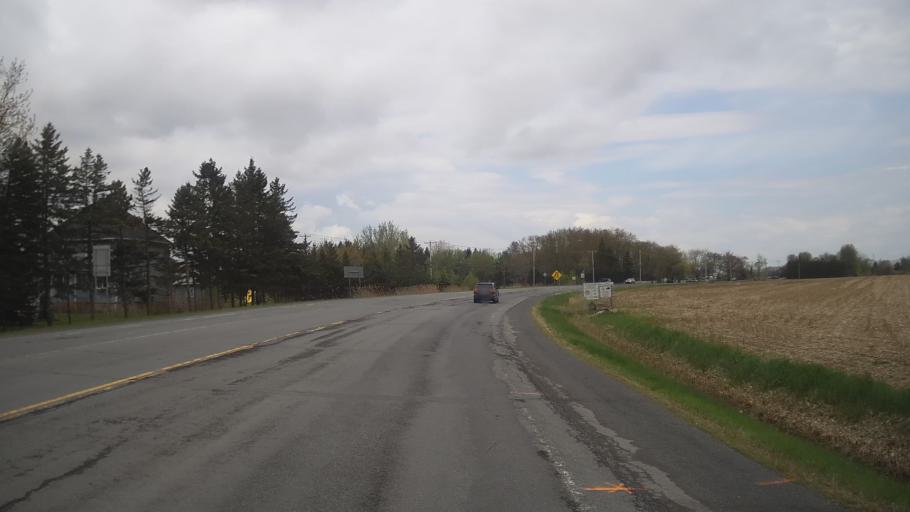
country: CA
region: Quebec
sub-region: Monteregie
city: Saint-Jean-sur-Richelieu
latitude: 45.3147
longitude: -73.1906
